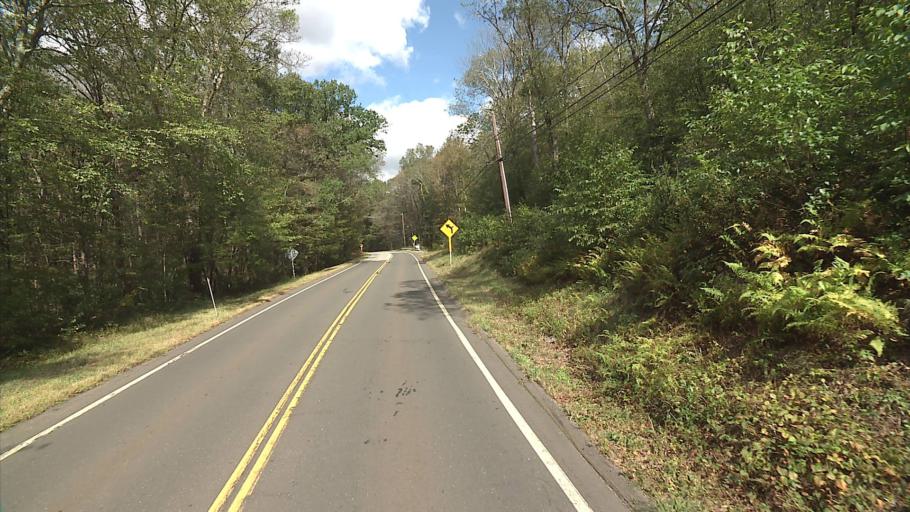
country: US
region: Connecticut
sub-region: Middlesex County
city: Durham
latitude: 41.4341
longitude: -72.6439
